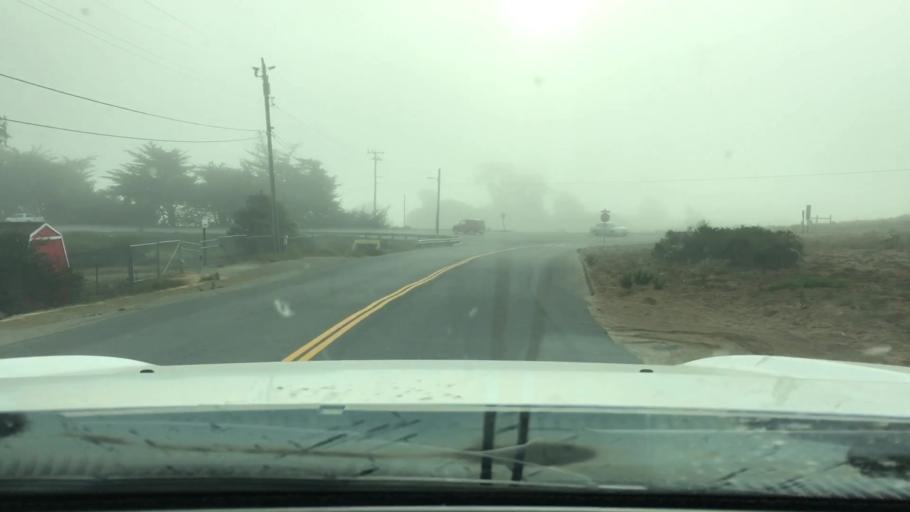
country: US
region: California
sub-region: San Luis Obispo County
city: Los Osos
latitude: 35.3221
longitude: -120.8256
